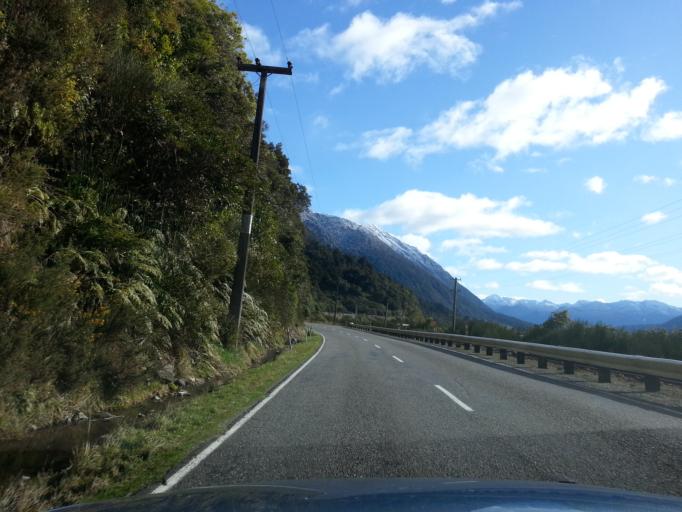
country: NZ
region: West Coast
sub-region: Grey District
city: Greymouth
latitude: -42.7634
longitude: 171.5973
